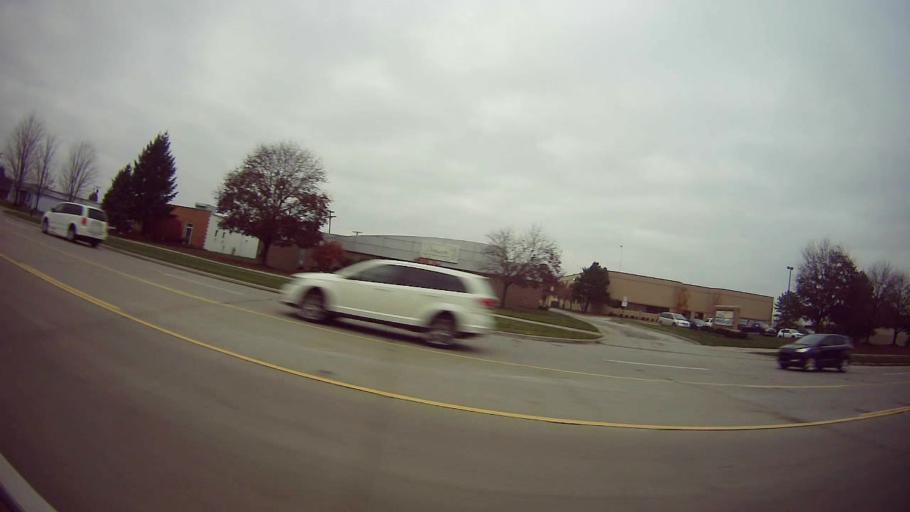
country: US
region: Michigan
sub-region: Oakland County
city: Madison Heights
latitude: 42.5369
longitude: -83.0869
